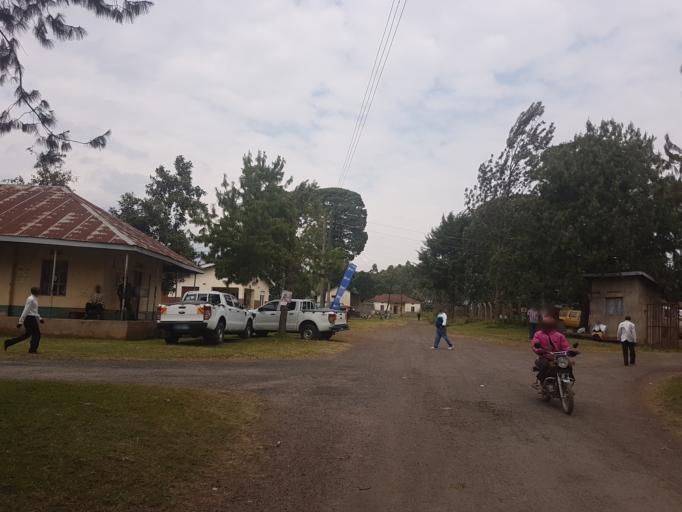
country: UG
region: Western Region
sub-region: Kisoro District
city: Kisoro
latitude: -1.2834
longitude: 29.6978
